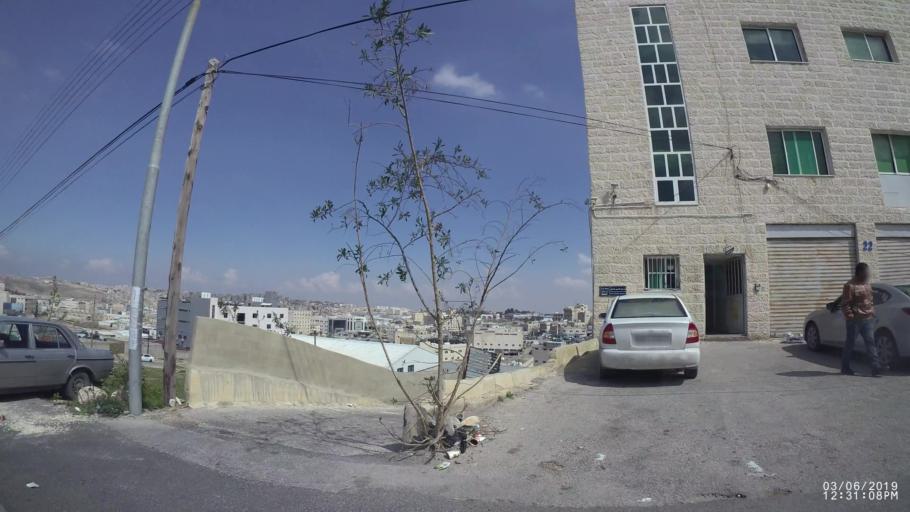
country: JO
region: Zarqa
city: Russeifa
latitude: 31.9971
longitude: 35.9977
